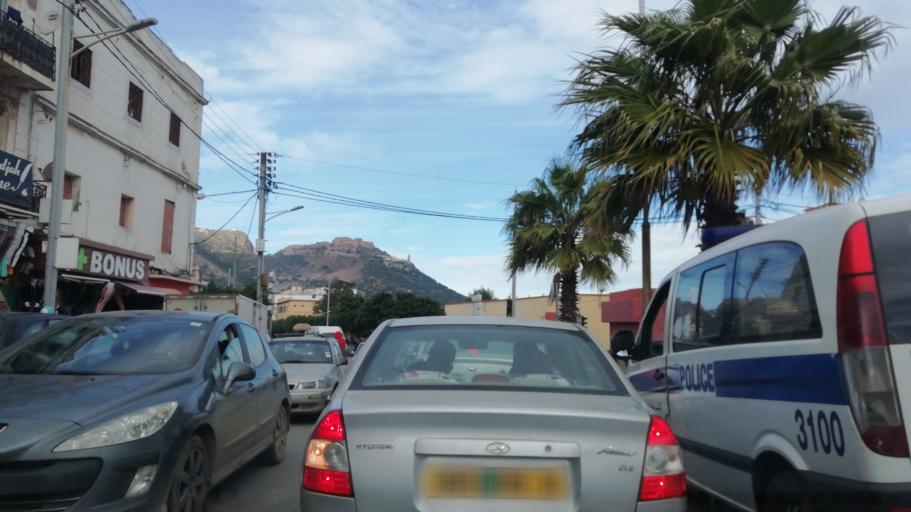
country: DZ
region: Oran
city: Oran
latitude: 35.6962
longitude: -0.6481
